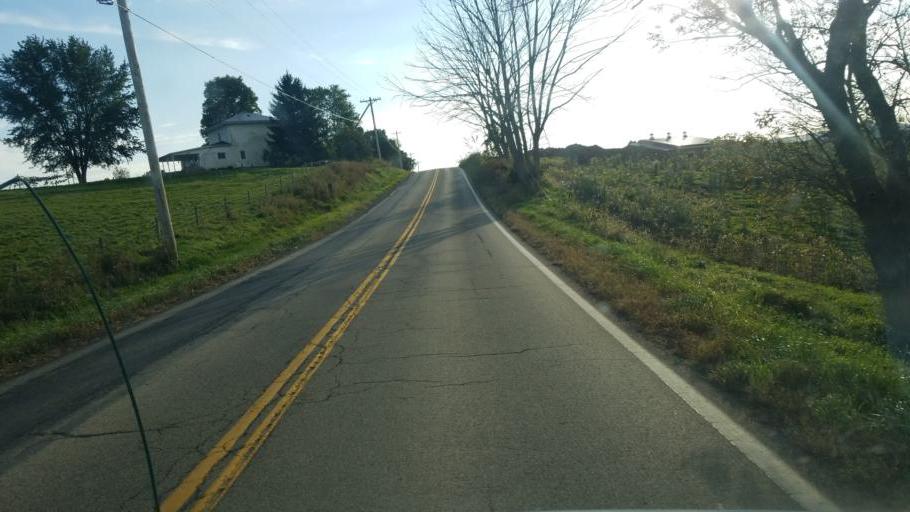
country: US
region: Ohio
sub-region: Wayne County
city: Shreve
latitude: 40.6161
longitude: -82.0961
